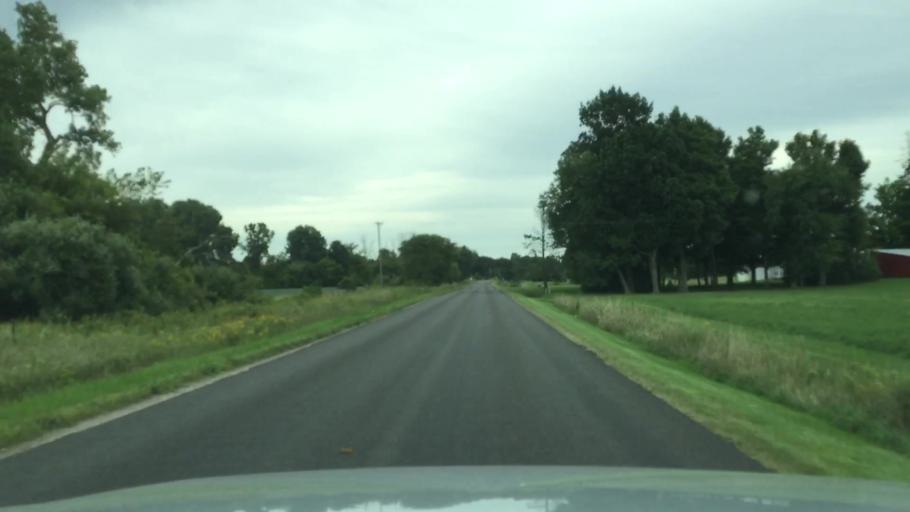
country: US
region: Michigan
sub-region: Shiawassee County
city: Durand
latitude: 42.8660
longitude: -84.0481
